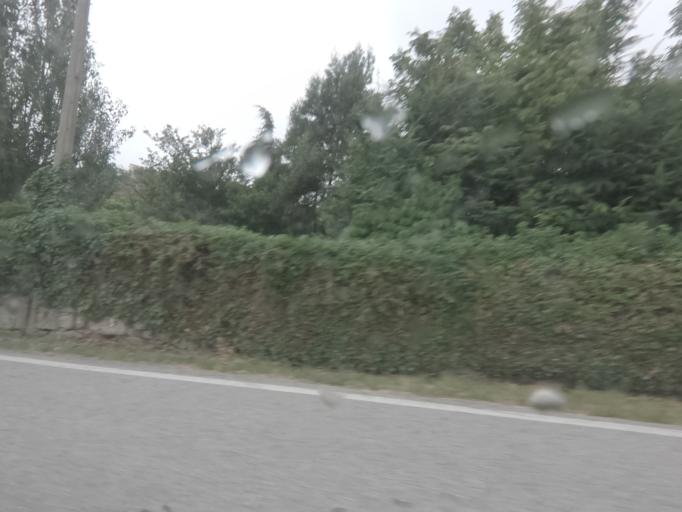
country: PT
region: Viseu
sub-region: Armamar
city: Armamar
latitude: 41.1144
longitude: -7.7161
